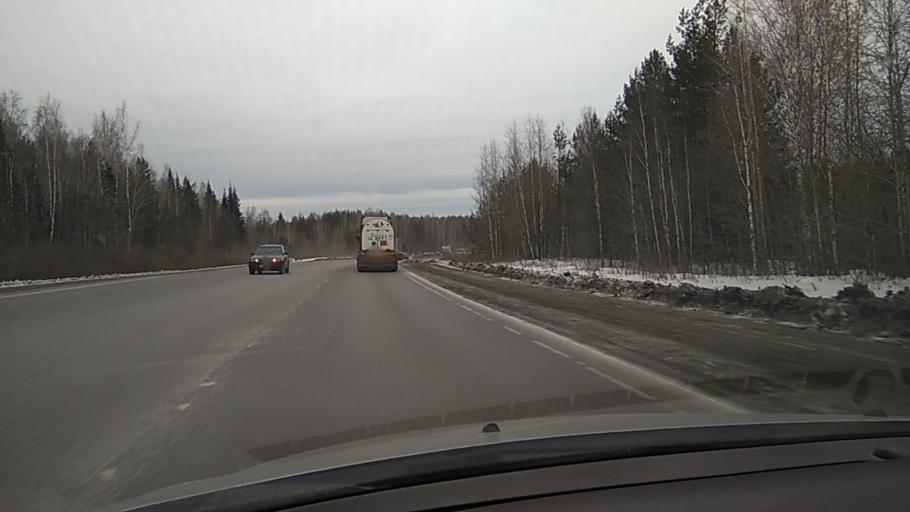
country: RU
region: Sverdlovsk
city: Talitsa
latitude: 56.8286
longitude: 59.9923
